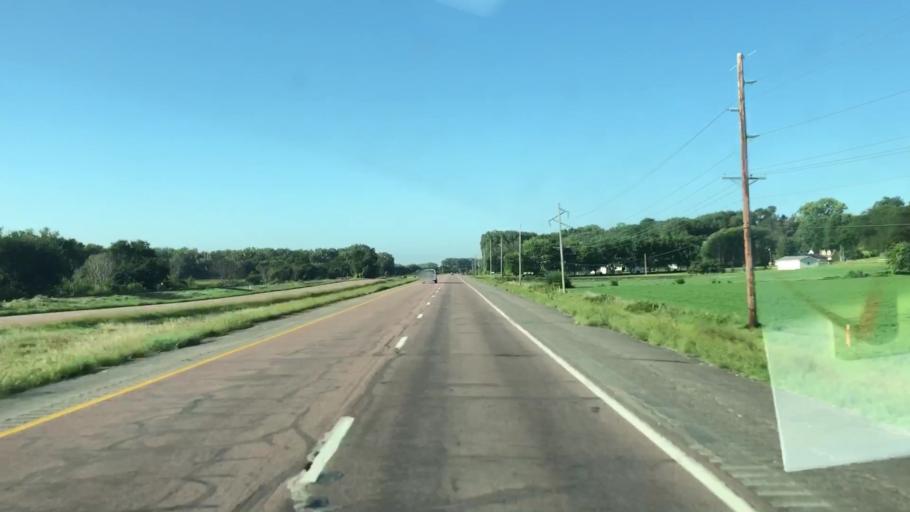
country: US
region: Iowa
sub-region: Woodbury County
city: Sioux City
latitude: 42.5754
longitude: -96.3175
